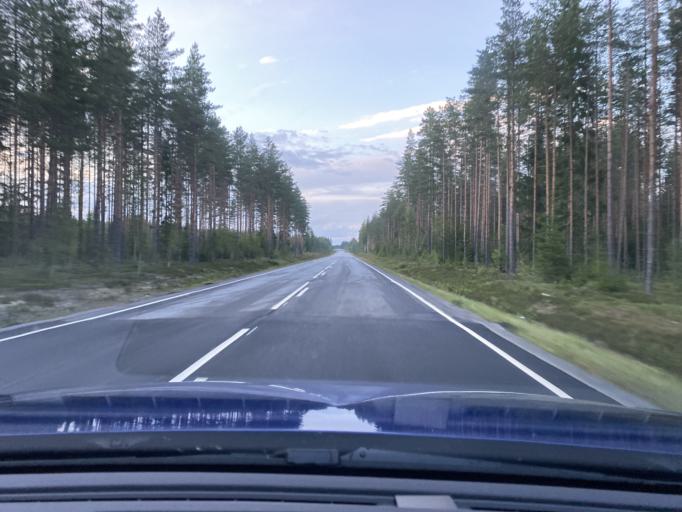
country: FI
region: Satakunta
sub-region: Pohjois-Satakunta
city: Honkajoki
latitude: 62.0258
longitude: 22.2311
